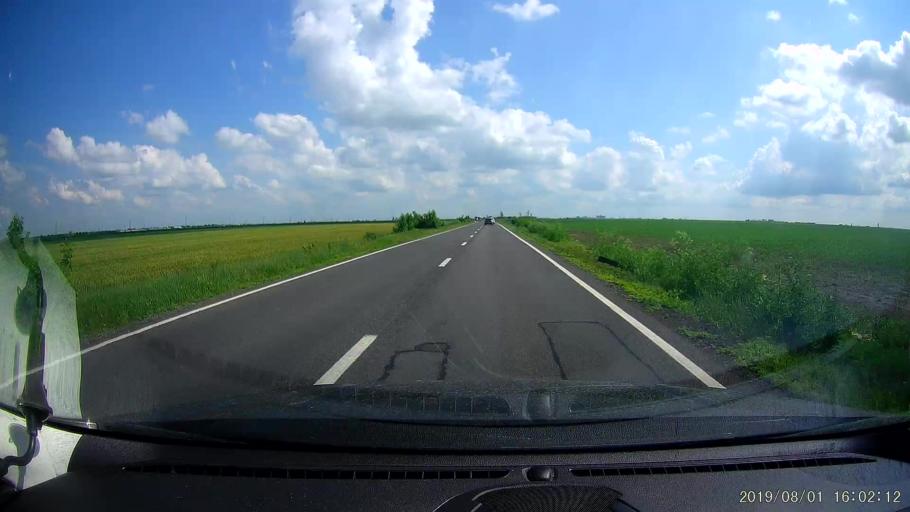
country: RO
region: Ialomita
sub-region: Comuna Ciulnita
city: Ciulnita
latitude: 44.4944
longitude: 27.3881
